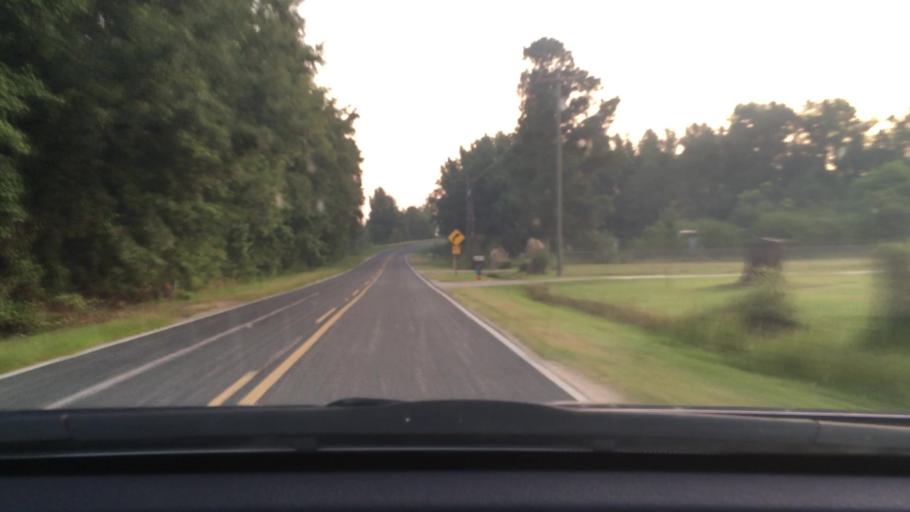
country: US
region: South Carolina
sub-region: Lee County
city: Bishopville
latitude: 34.1907
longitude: -80.1415
